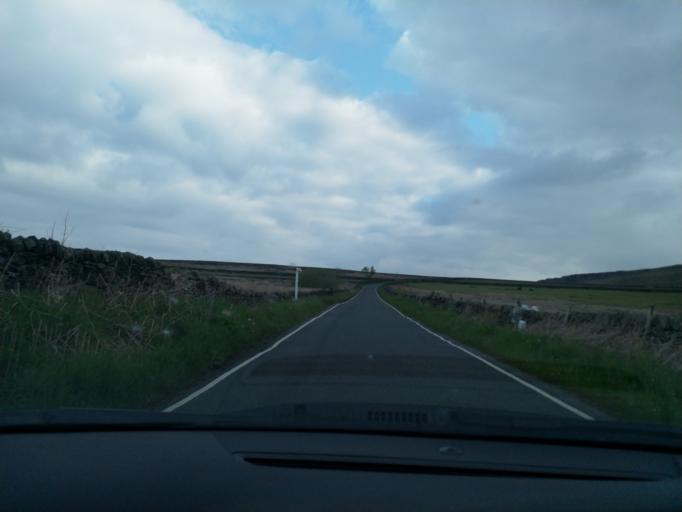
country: GB
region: England
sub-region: Derbyshire
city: Hathersage
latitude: 53.3360
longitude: -1.6321
